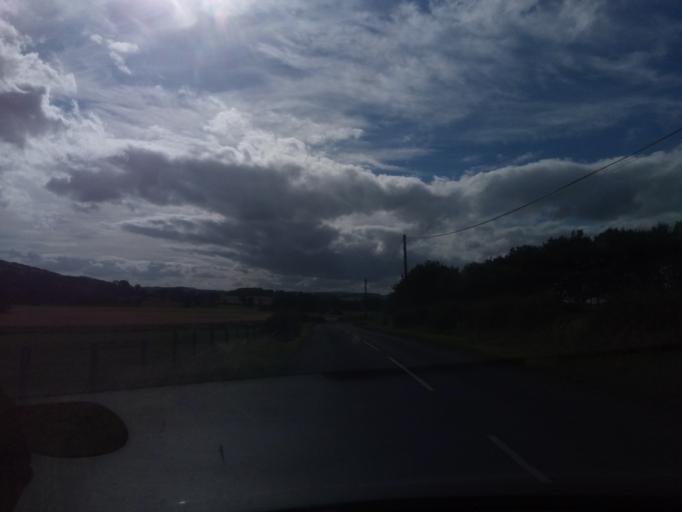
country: GB
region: Scotland
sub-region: The Scottish Borders
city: Coldstream
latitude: 55.5949
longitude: -2.2178
